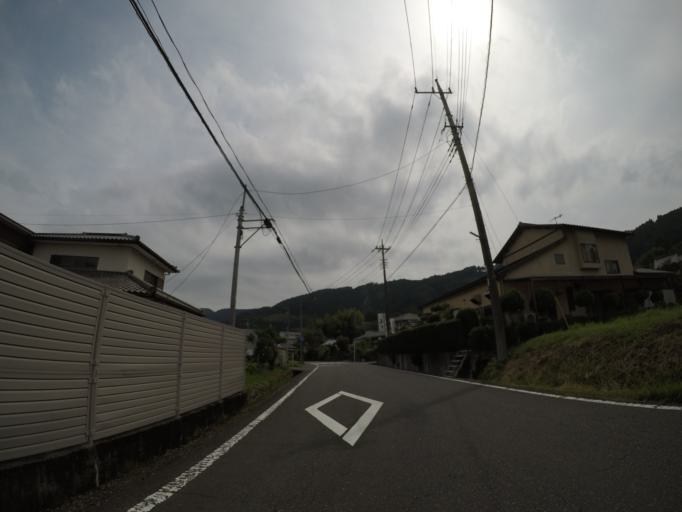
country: JP
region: Shizuoka
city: Fujinomiya
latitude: 35.2599
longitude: 138.5543
